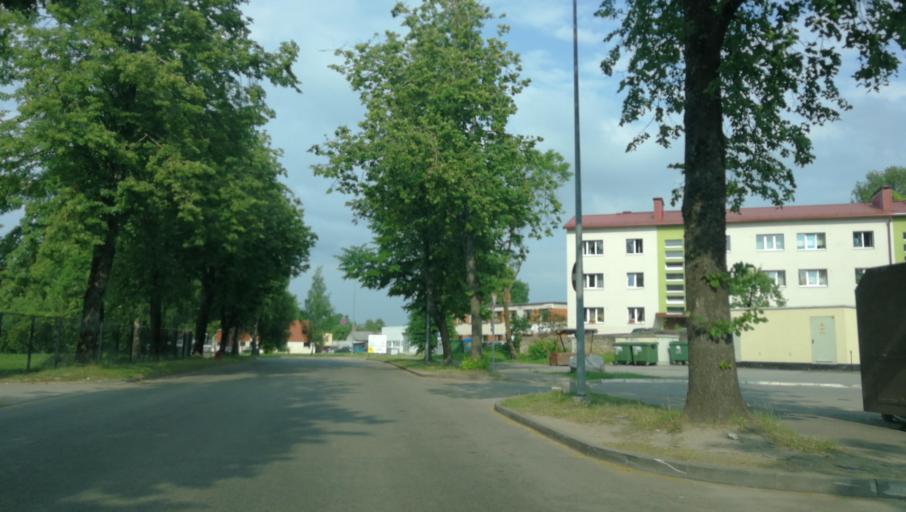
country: LV
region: Cesu Rajons
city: Cesis
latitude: 57.3149
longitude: 25.2818
